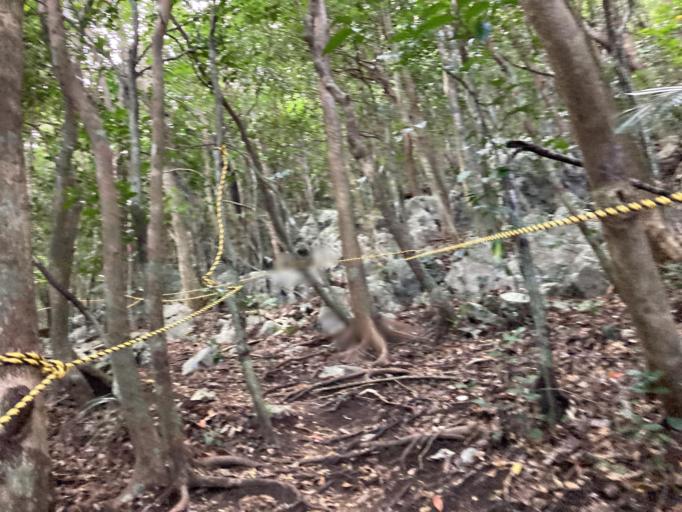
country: JP
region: Okinawa
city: Nago
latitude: 26.8554
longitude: 128.2587
